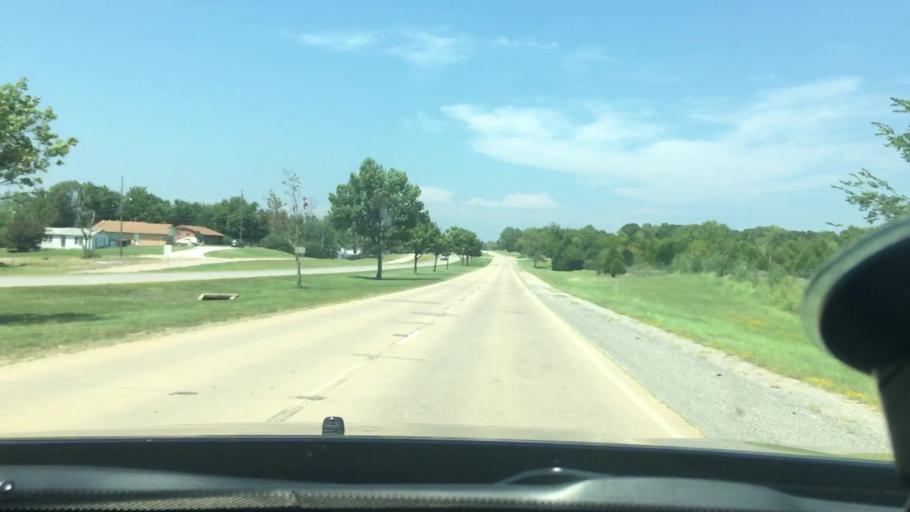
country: US
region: Oklahoma
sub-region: Pontotoc County
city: Ada
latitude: 34.8070
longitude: -96.6782
